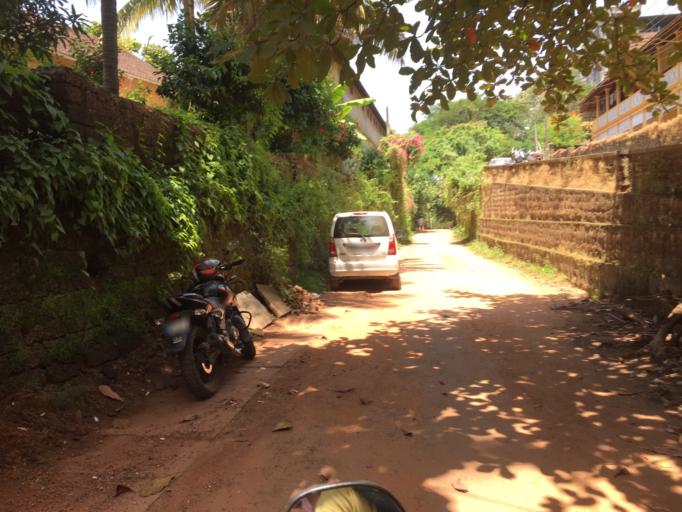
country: IN
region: Karnataka
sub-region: Dakshina Kannada
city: Mangalore
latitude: 12.8736
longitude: 74.8419
